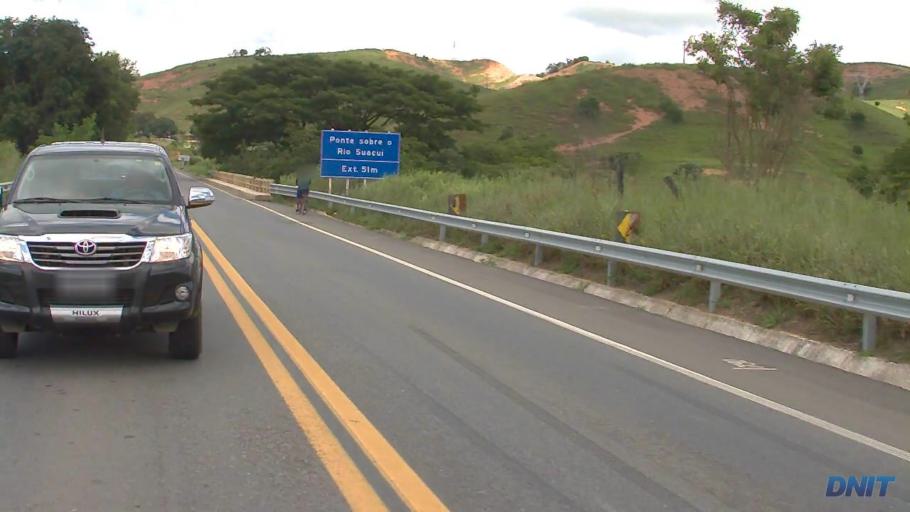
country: BR
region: Minas Gerais
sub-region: Governador Valadares
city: Governador Valadares
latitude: -18.9611
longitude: -42.0759
